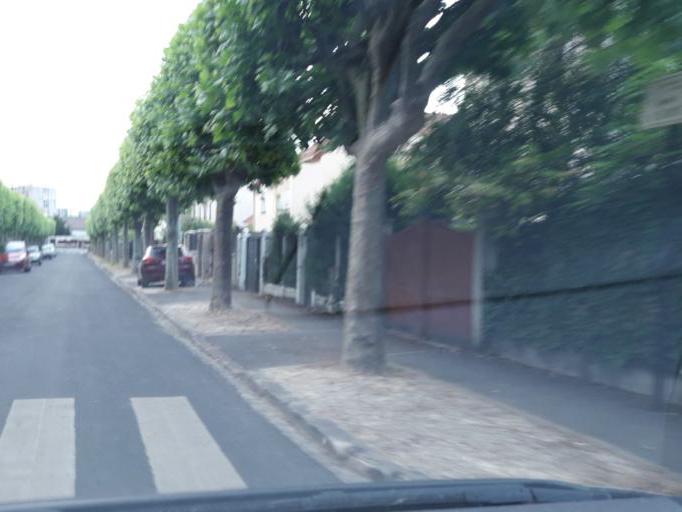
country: FR
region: Ile-de-France
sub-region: Departement de l'Essonne
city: Morsang-sur-Orge
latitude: 48.6587
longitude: 2.3580
